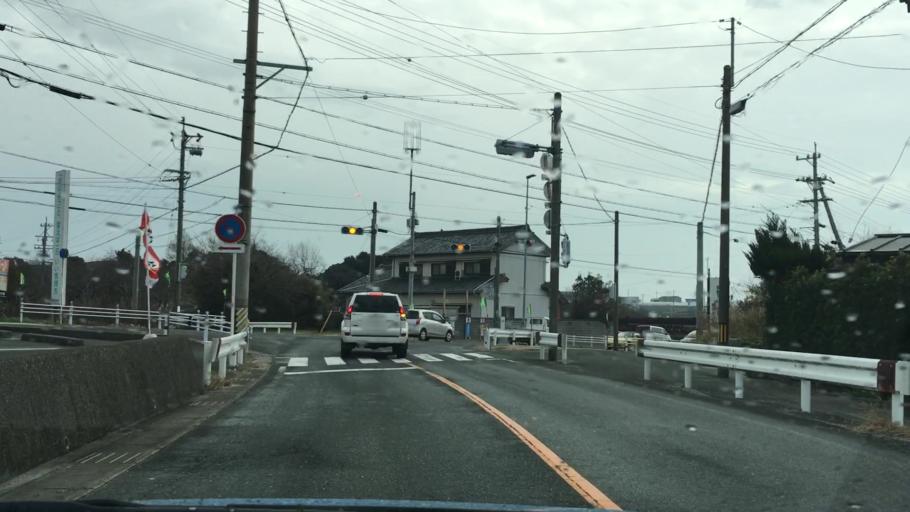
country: JP
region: Aichi
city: Tahara
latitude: 34.6959
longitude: 137.2769
